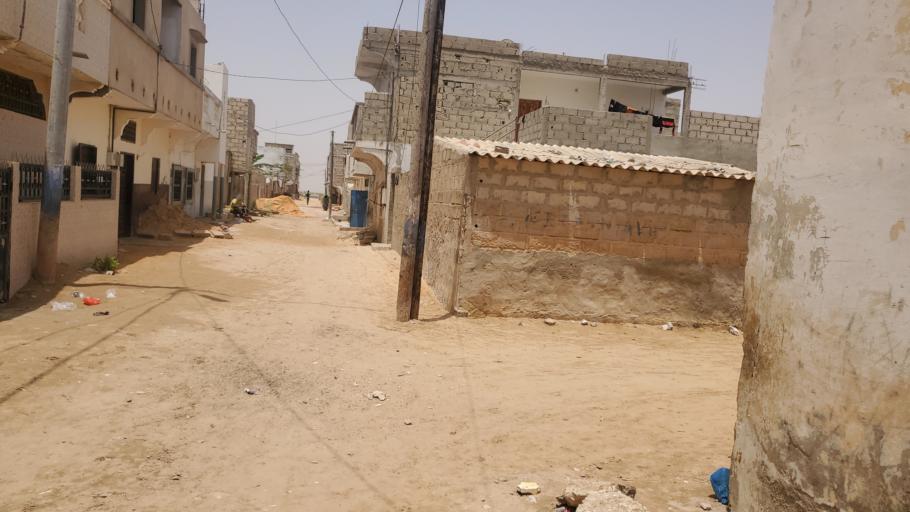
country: SN
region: Saint-Louis
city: Saint-Louis
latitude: 16.0152
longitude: -16.4851
